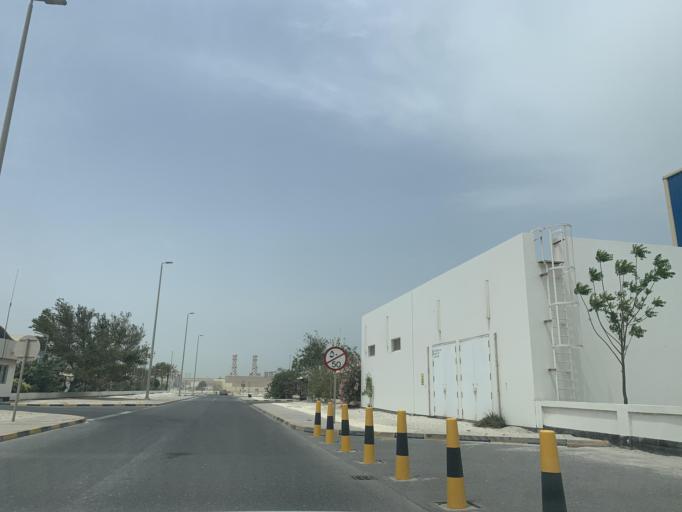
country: BH
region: Muharraq
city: Al Hadd
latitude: 26.2181
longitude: 50.6694
